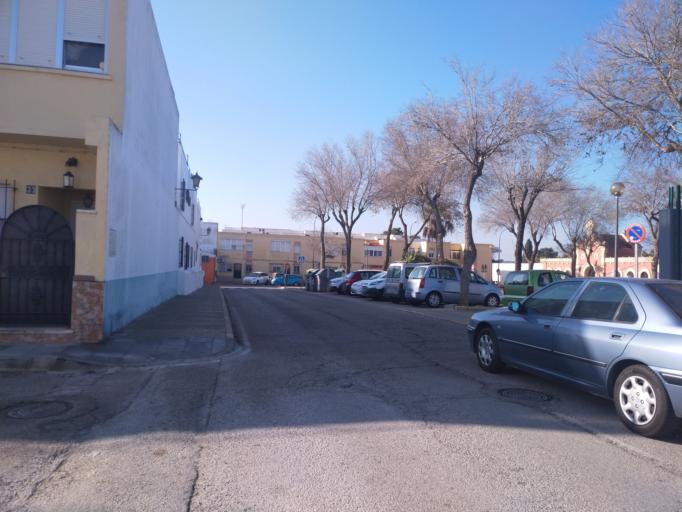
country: ES
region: Andalusia
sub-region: Provincia de Cadiz
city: San Fernando
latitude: 36.4691
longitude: -6.2025
